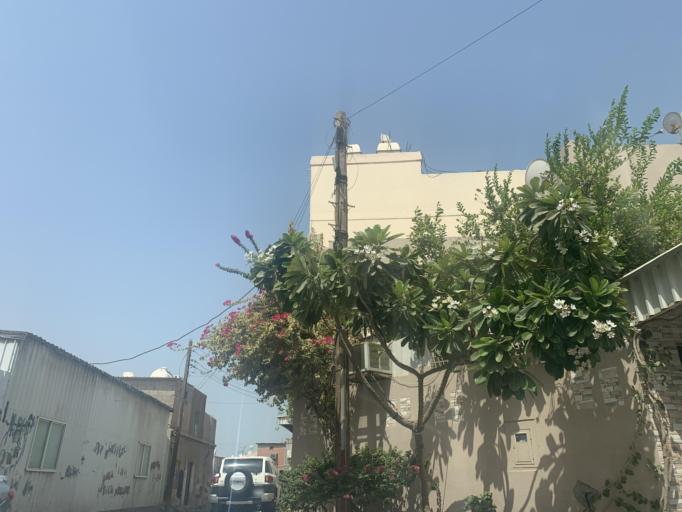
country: BH
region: Manama
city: Jidd Hafs
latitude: 26.2119
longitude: 50.4604
